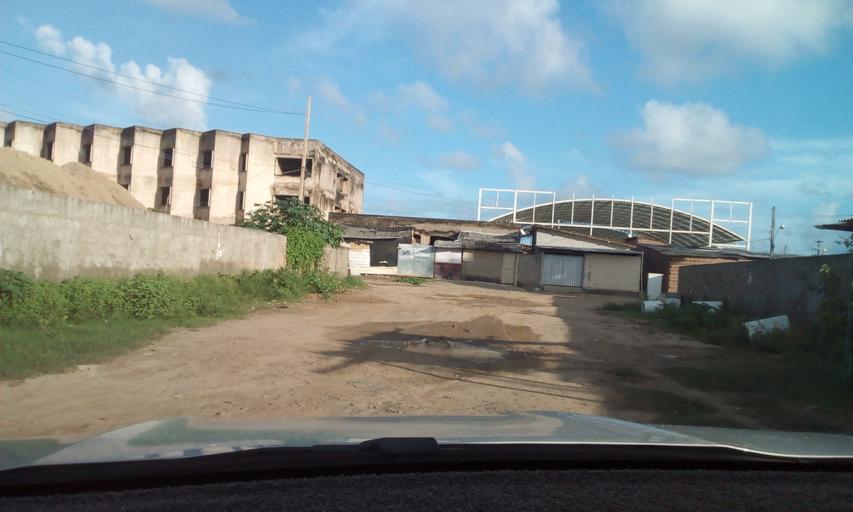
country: BR
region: Paraiba
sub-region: Joao Pessoa
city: Joao Pessoa
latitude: -7.1381
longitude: -34.8229
